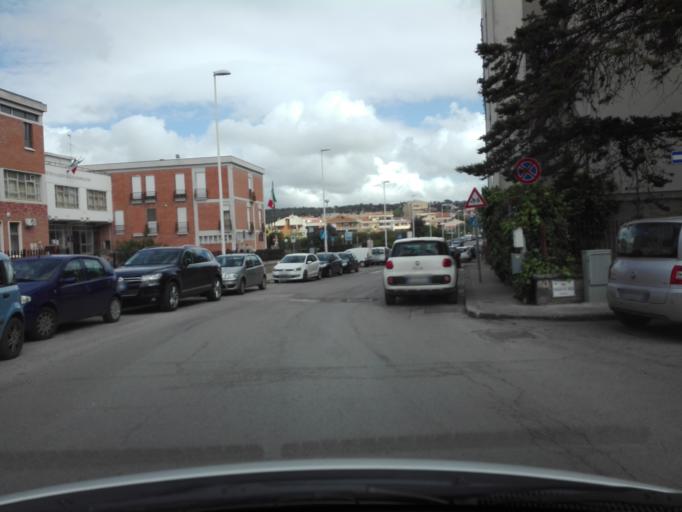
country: IT
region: Sardinia
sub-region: Provincia di Sassari
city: Sassari
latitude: 40.7244
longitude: 8.5772
